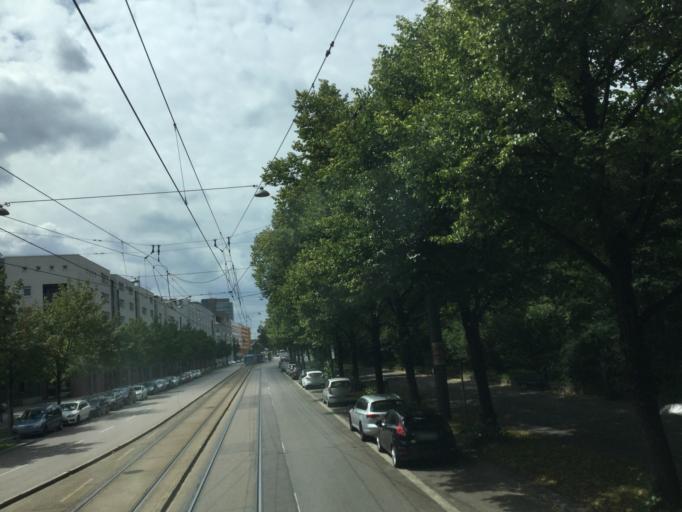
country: DE
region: Bavaria
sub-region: Upper Bavaria
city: Munich
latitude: 48.1444
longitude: 11.5448
